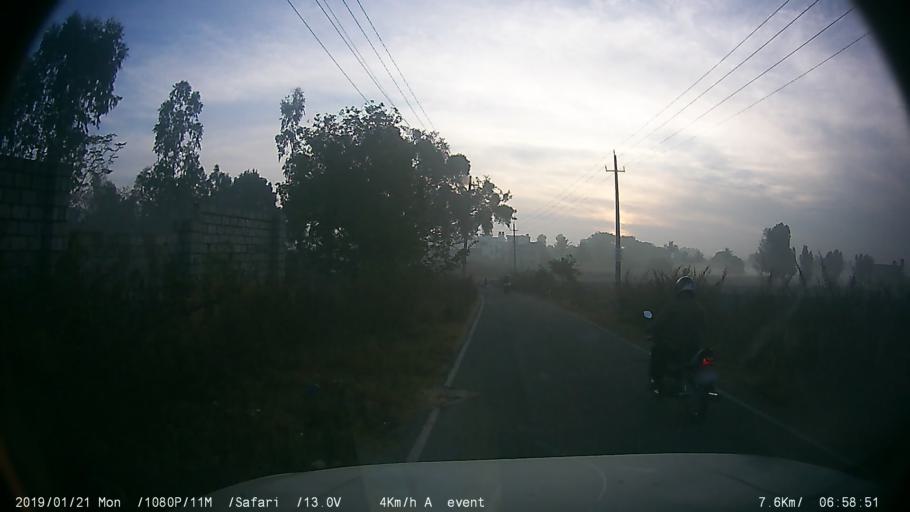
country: IN
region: Karnataka
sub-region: Bangalore Urban
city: Anekal
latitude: 12.8255
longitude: 77.6266
